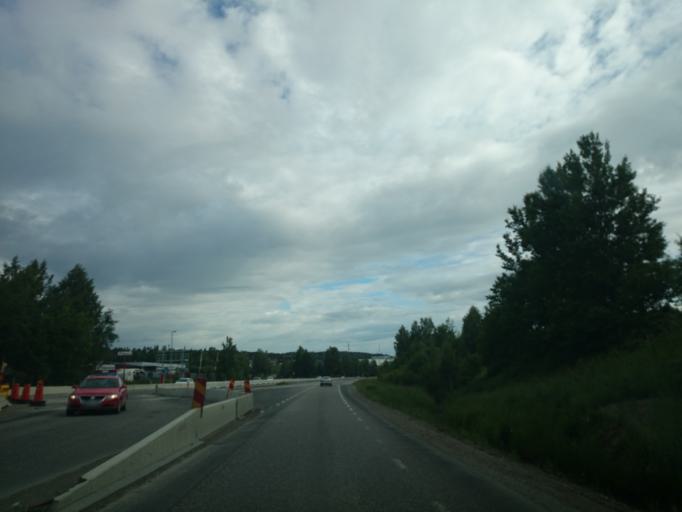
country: SE
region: Vaesternorrland
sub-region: Sundsvalls Kommun
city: Sundsvall
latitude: 62.4062
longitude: 17.3373
